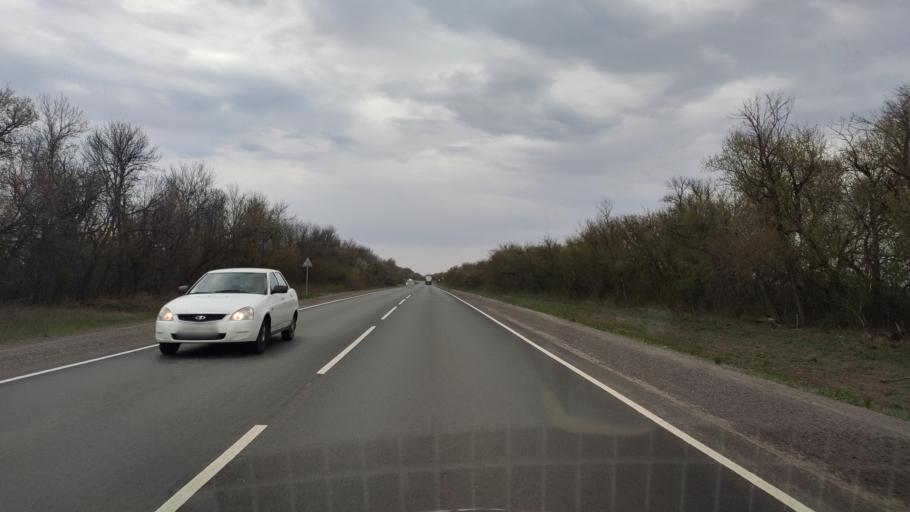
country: RU
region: Voronezj
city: Nizhnedevitsk
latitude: 51.6158
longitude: 38.6206
